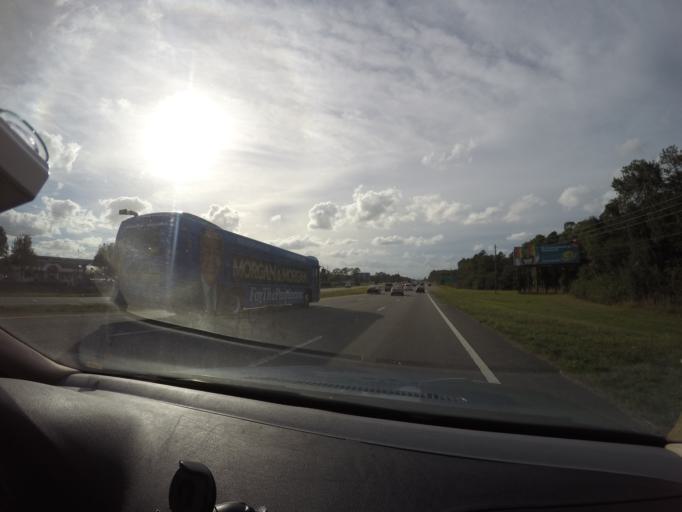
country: US
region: Florida
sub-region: Orange County
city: Oak Ridge
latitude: 28.4505
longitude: -81.4237
